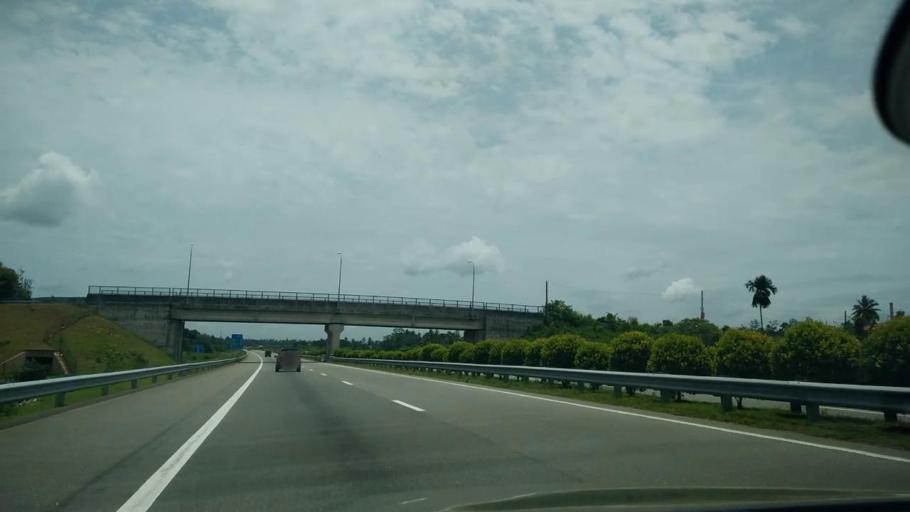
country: LK
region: Western
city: Homagama
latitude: 6.8732
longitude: 79.9780
